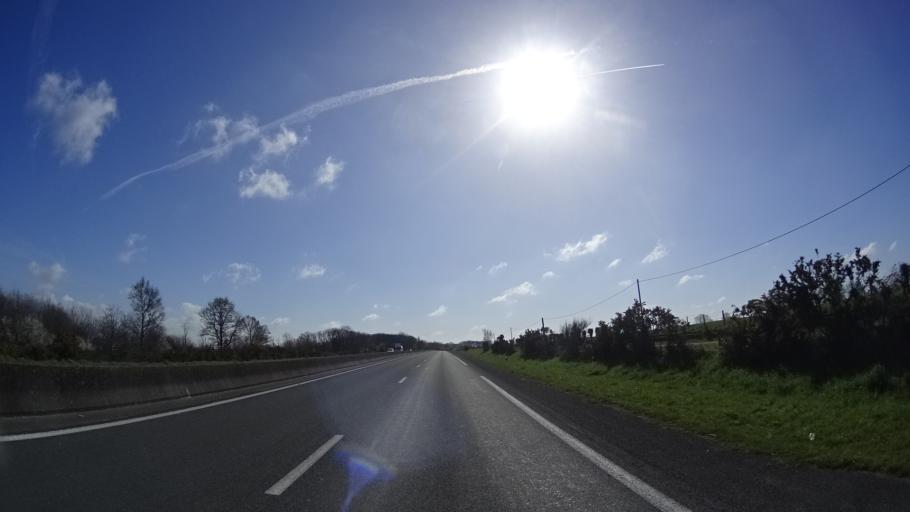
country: FR
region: Pays de la Loire
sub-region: Departement de Maine-et-Loire
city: Grez-Neuville
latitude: 47.6631
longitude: -0.7651
